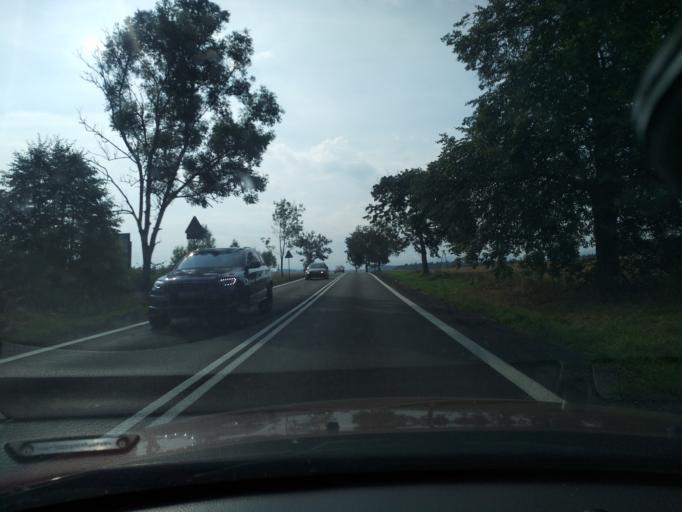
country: PL
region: Lower Silesian Voivodeship
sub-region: Powiat jeleniogorski
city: Stara Kamienica
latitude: 50.9463
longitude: 15.5877
